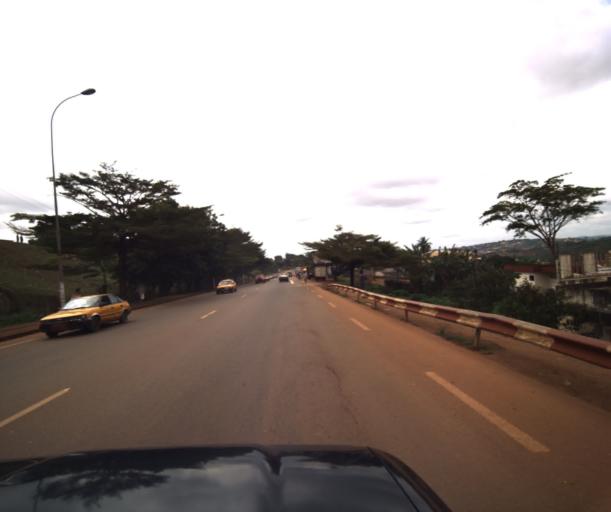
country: CM
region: Centre
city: Yaounde
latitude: 3.8332
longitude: 11.5190
